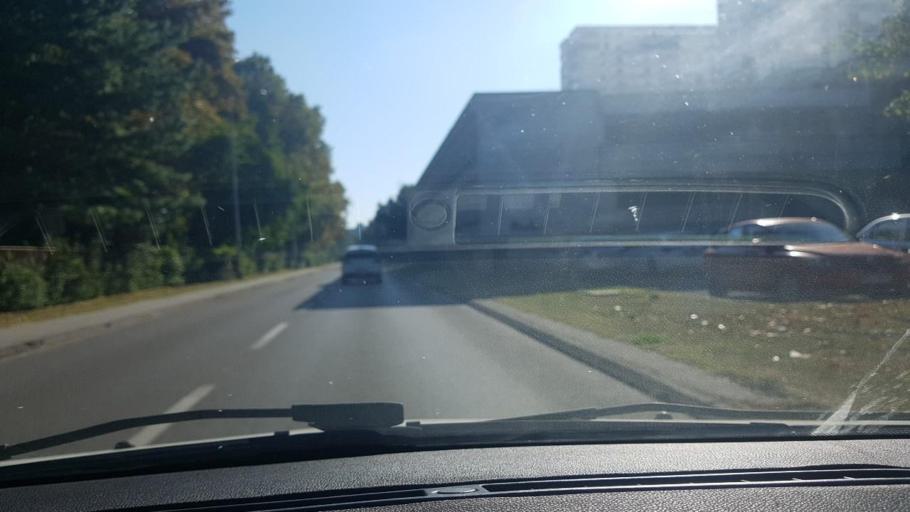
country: HR
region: Grad Zagreb
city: Novi Zagreb
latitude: 45.7736
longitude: 15.9754
